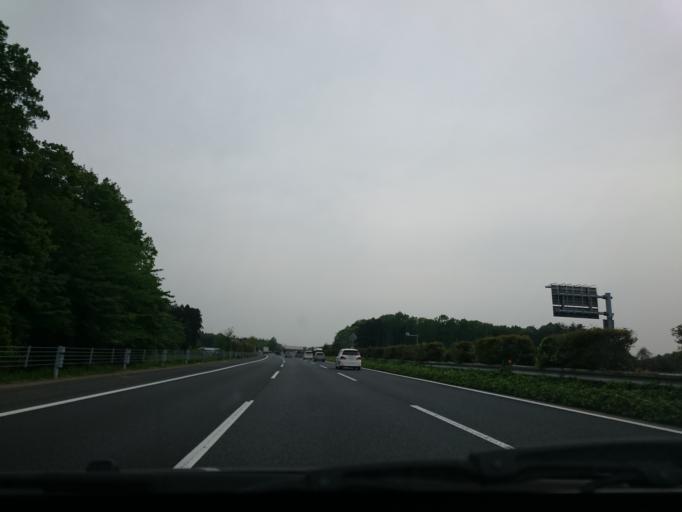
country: JP
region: Tochigi
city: Utsunomiya-shi
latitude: 36.6253
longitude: 139.8433
